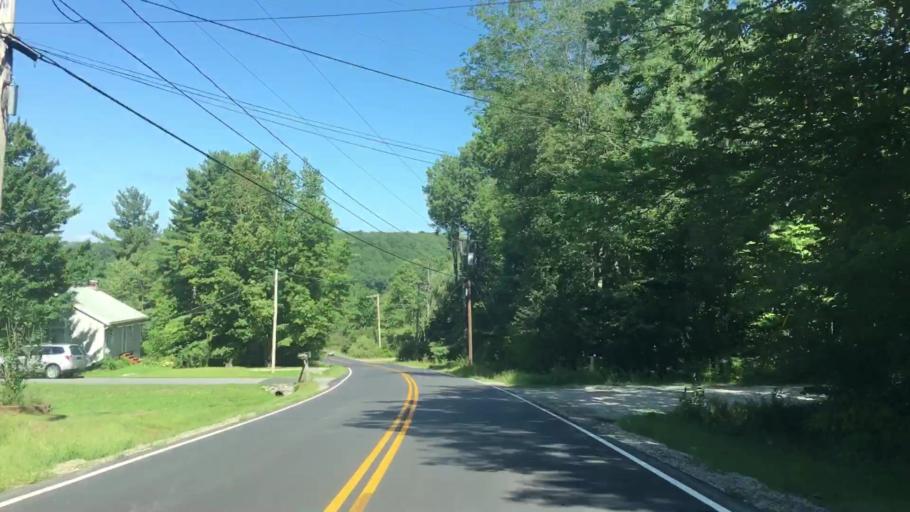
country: US
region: Maine
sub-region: Sagadahoc County
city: Topsham
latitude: 43.9755
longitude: -69.9792
